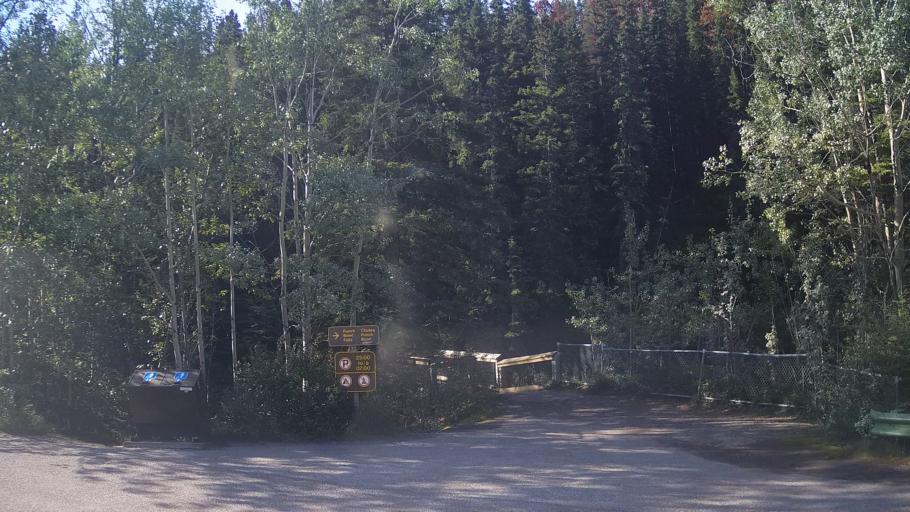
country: CA
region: Alberta
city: Jasper Park Lodge
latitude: 53.1992
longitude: -117.9224
